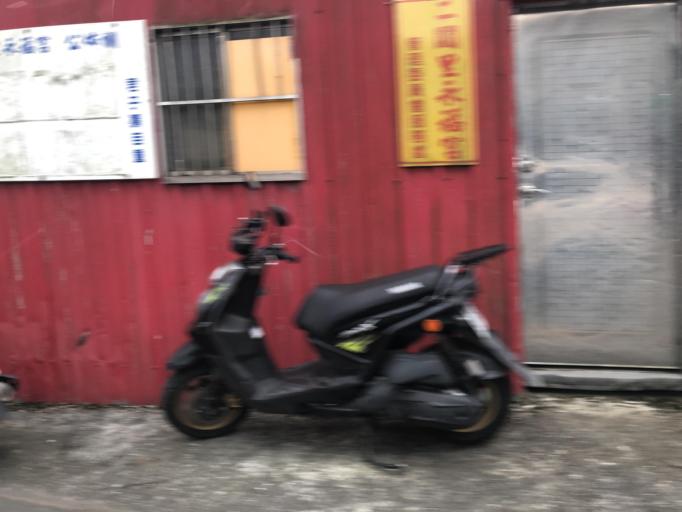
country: TW
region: Taiwan
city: Daxi
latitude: 24.9086
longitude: 121.3598
